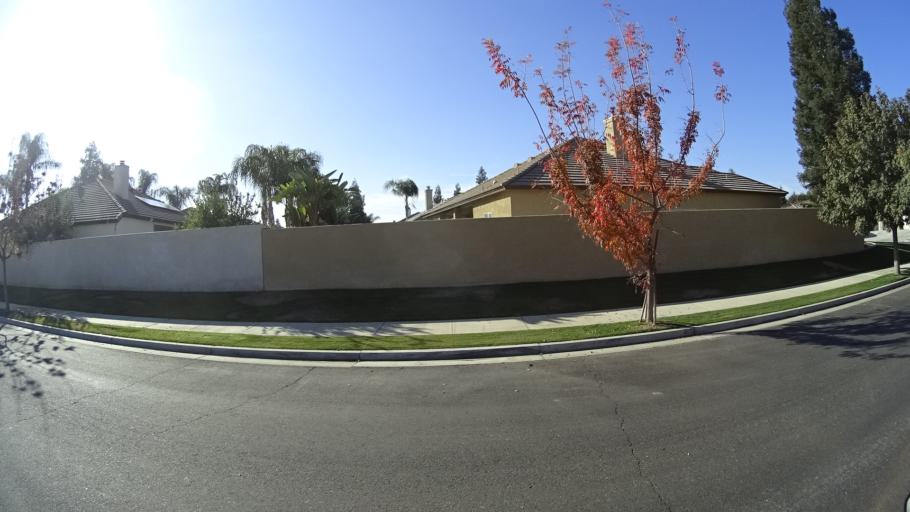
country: US
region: California
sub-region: Kern County
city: Rosedale
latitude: 35.3267
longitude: -119.1343
